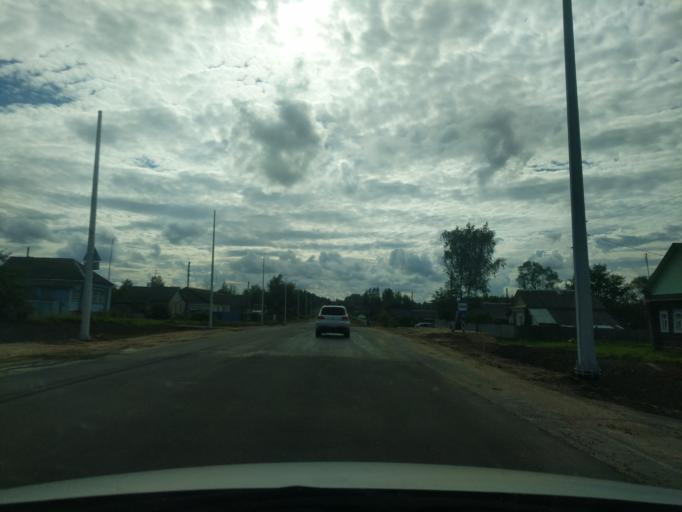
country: RU
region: Jaroslavl
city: Levashevo
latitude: 57.6532
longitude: 40.5571
